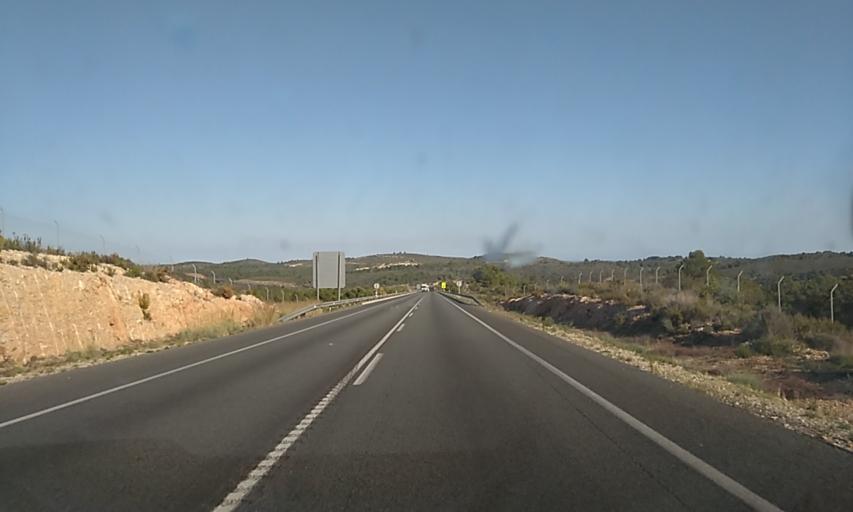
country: ES
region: Valencia
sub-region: Provincia de Castello
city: Torreblanca
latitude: 40.2113
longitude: 0.1265
